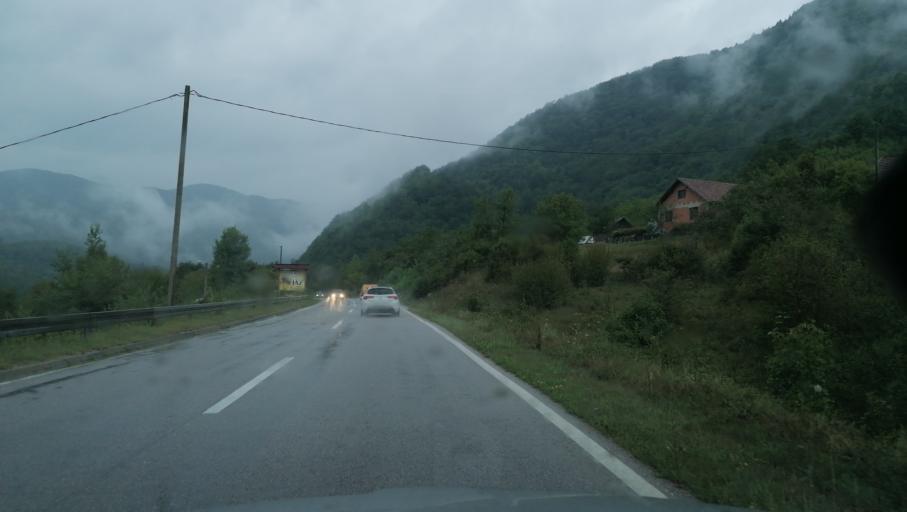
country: BA
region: Republika Srpska
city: Visegrad
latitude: 43.7159
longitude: 19.1681
